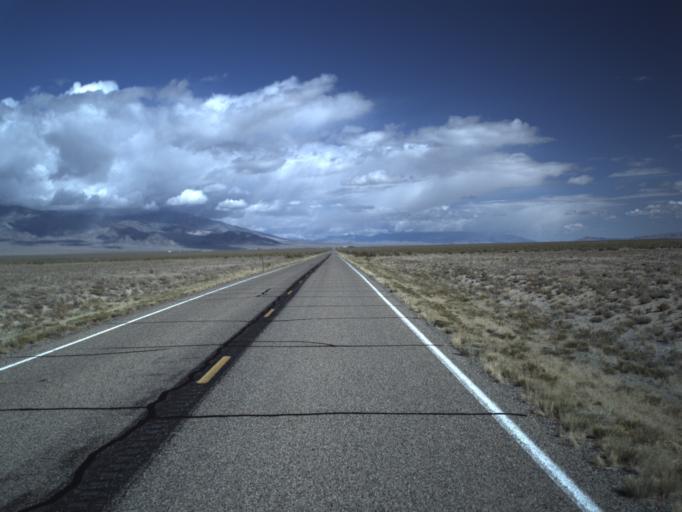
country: US
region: Nevada
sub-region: White Pine County
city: McGill
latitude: 38.9900
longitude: -114.0344
